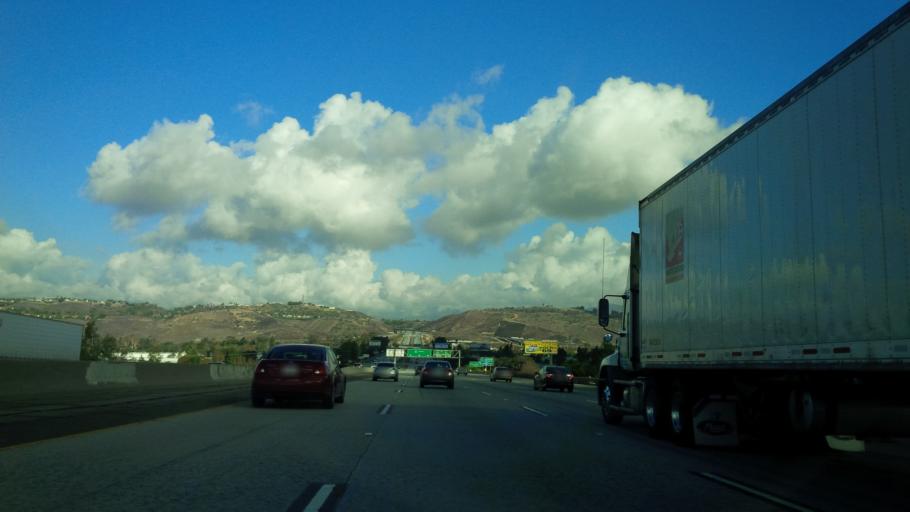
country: US
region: California
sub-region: Los Angeles County
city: Diamond Bar
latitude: 34.0484
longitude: -117.8012
